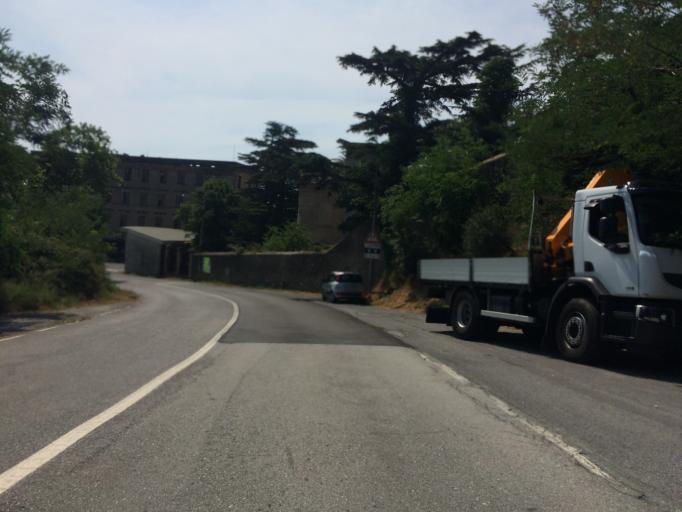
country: IT
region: Liguria
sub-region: Provincia di Genova
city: Sciarborasca
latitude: 44.3927
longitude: 8.6257
